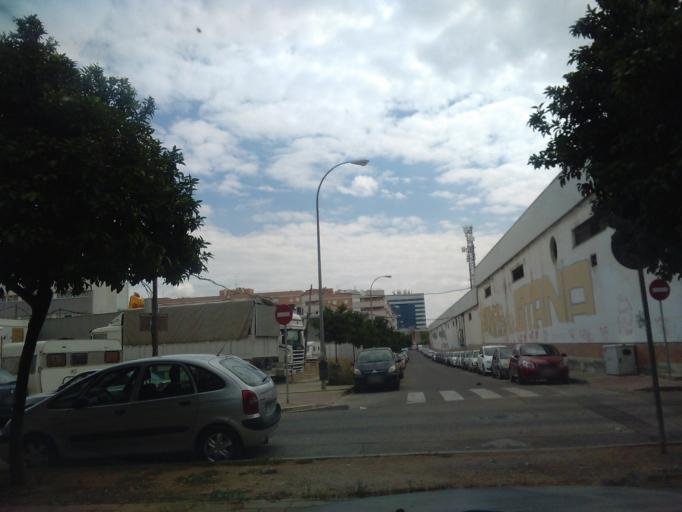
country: ES
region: Andalusia
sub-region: Provincia de Sevilla
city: Sevilla
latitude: 37.4103
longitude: -5.9284
